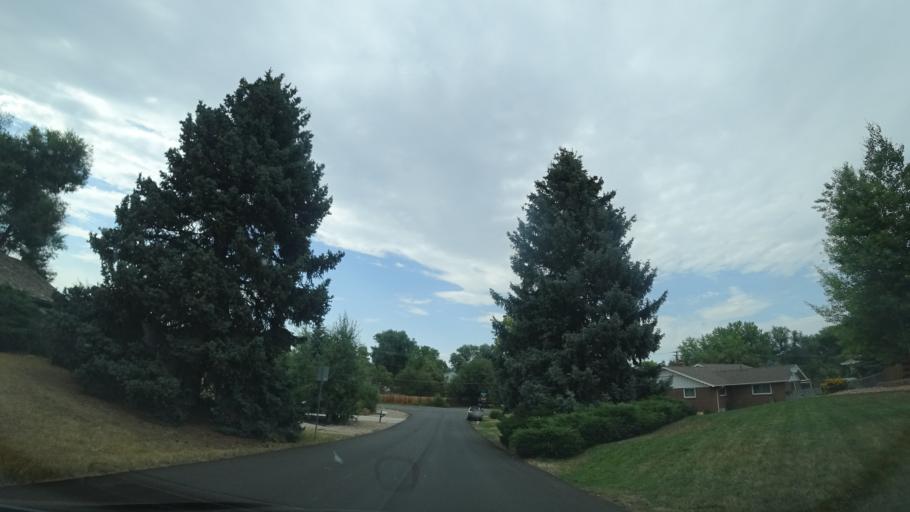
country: US
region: Colorado
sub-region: Jefferson County
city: Lakewood
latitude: 39.7178
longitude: -105.0873
